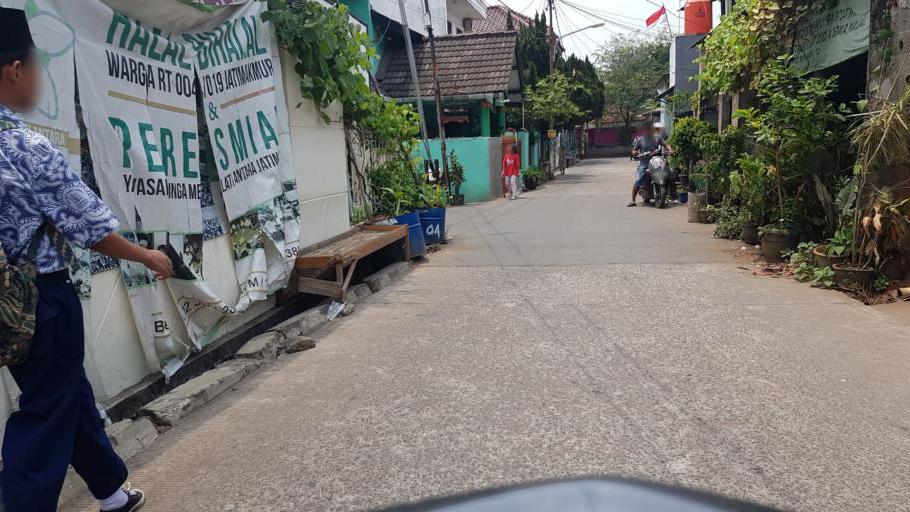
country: ID
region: West Java
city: Bekasi
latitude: -6.2779
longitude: 106.9306
